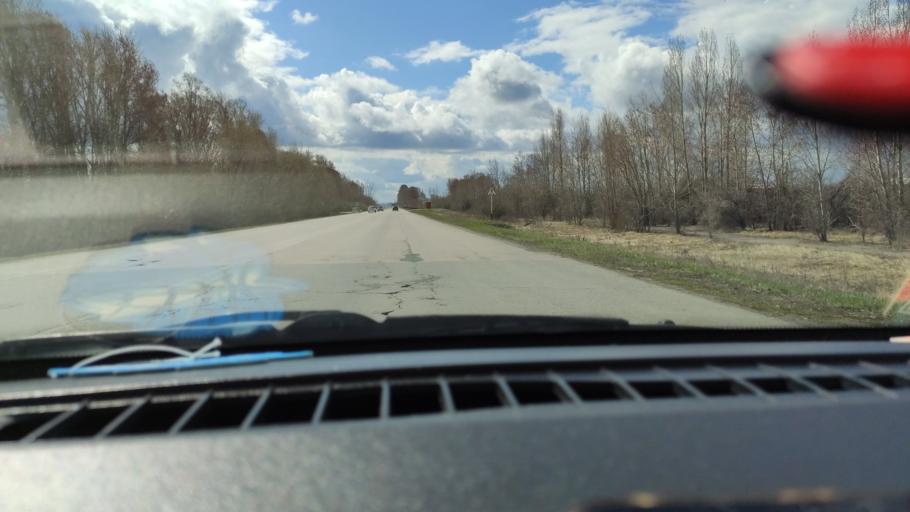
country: RU
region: Samara
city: Tol'yatti
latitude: 53.6957
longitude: 49.4194
